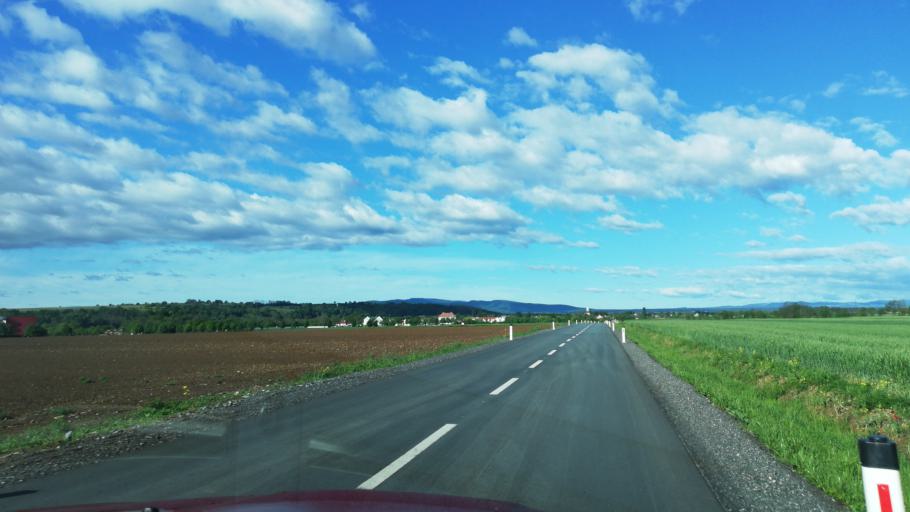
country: AT
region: Burgenland
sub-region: Politischer Bezirk Oberpullendorf
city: Lutzmannsburg
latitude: 47.4704
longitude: 16.6599
